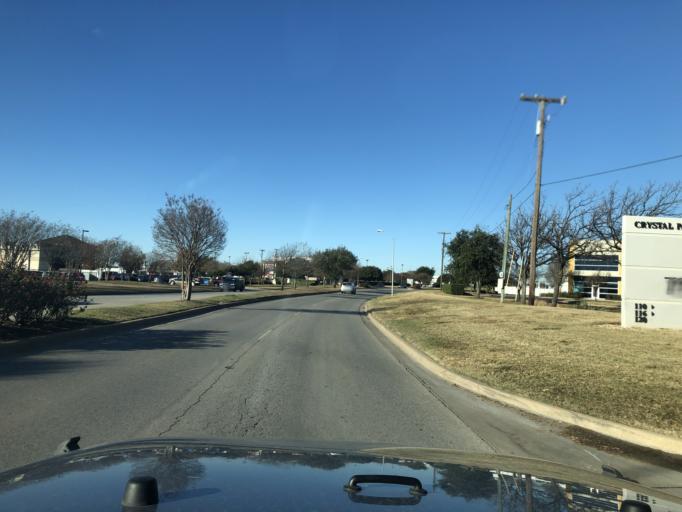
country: US
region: Texas
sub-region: Williamson County
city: Round Rock
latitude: 30.5337
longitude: -97.6859
